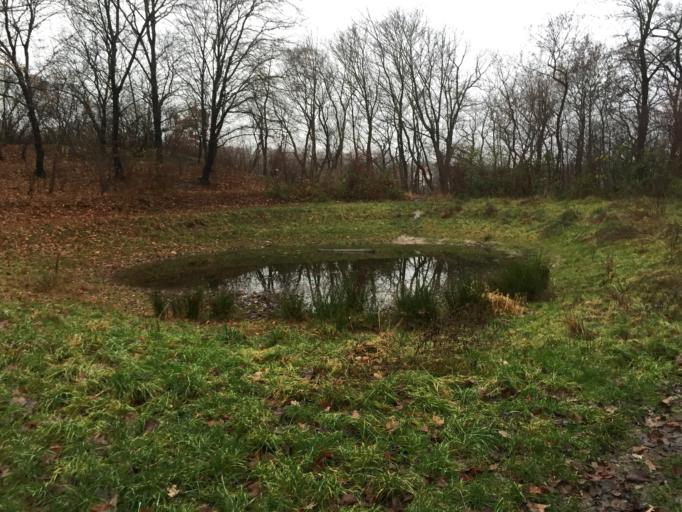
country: DE
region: Saxony
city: Bannewitz
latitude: 51.0255
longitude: 13.7030
